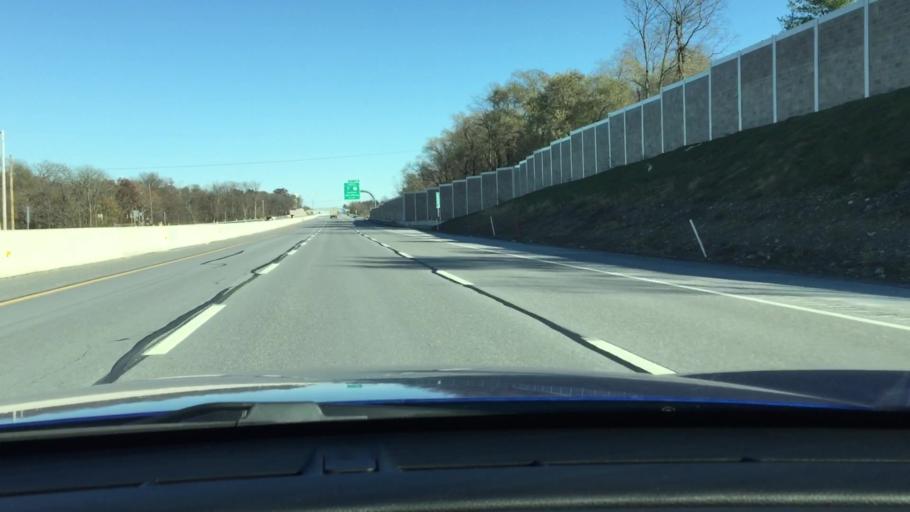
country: US
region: Pennsylvania
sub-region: Cumberland County
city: Carlisle
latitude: 40.2191
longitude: -77.1928
